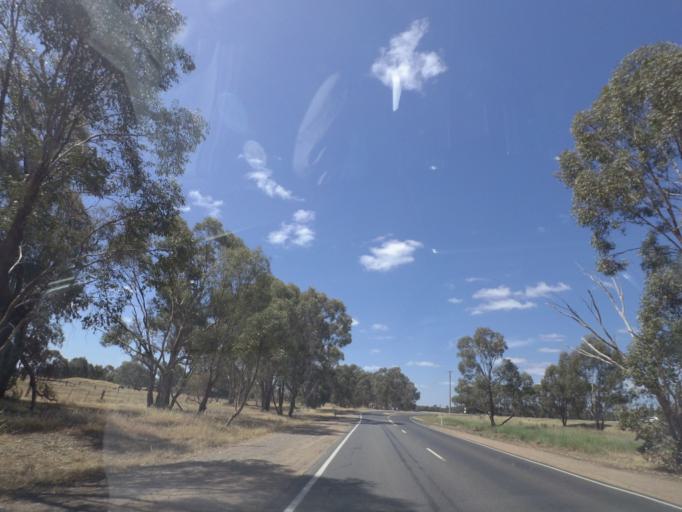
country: AU
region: Victoria
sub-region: Wangaratta
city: Wangaratta
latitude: -36.4077
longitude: 146.2714
